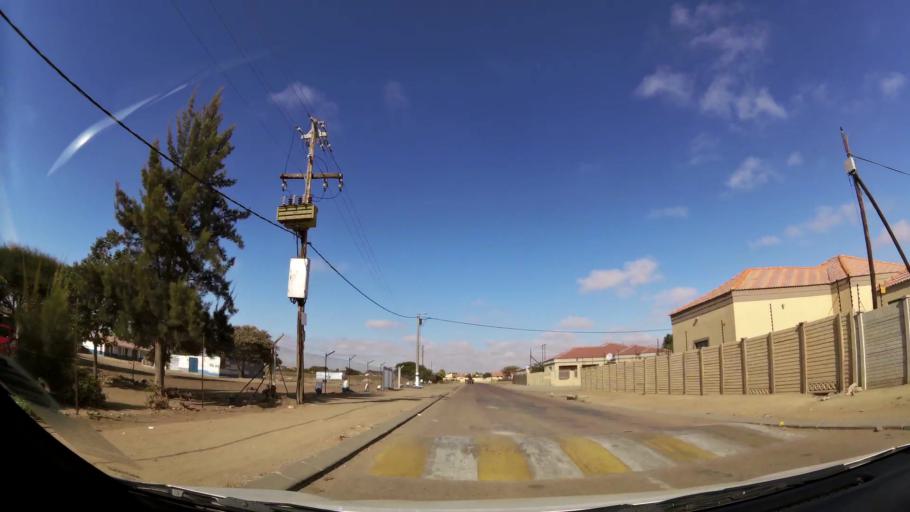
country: ZA
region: Limpopo
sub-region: Capricorn District Municipality
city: Polokwane
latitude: -23.8507
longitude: 29.4049
